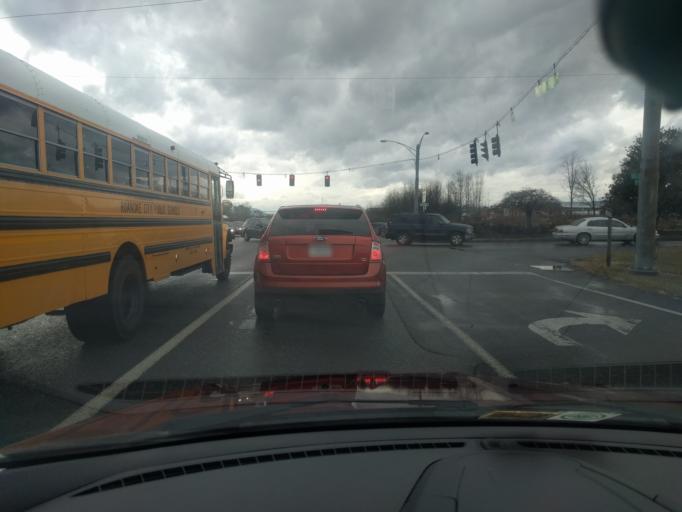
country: US
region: Virginia
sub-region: Roanoke County
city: Hollins
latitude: 37.3304
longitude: -79.9831
